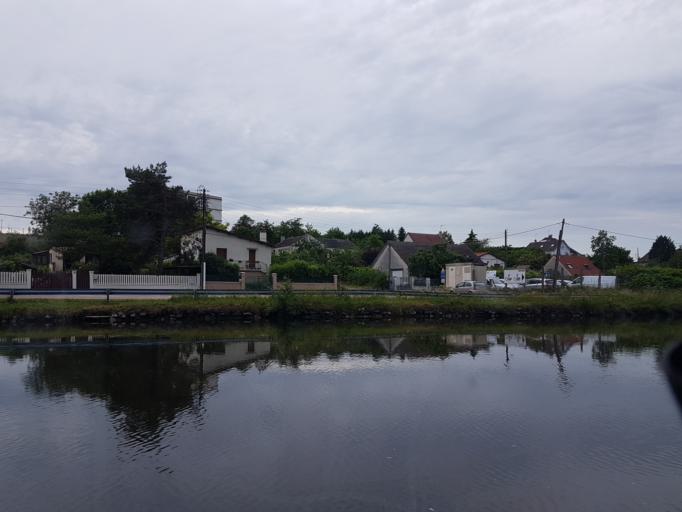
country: FR
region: Bourgogne
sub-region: Departement de l'Yonne
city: Auxerre
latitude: 47.8090
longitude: 3.5766
